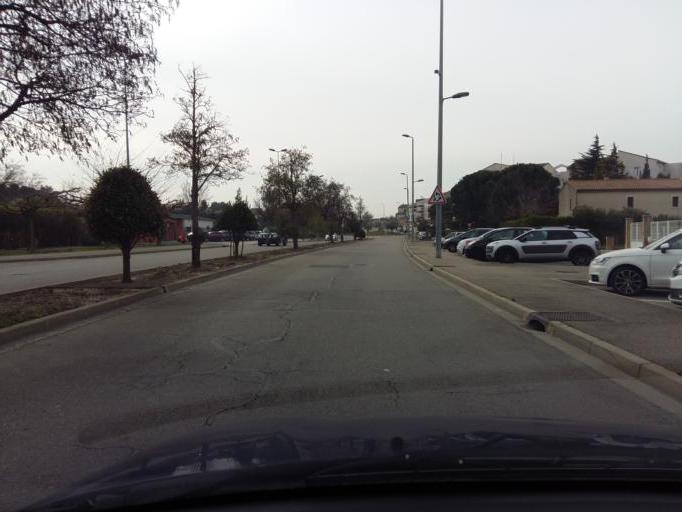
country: FR
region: Provence-Alpes-Cote d'Azur
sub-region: Departement des Bouches-du-Rhone
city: Chateaurenard
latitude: 43.8799
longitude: 4.8501
